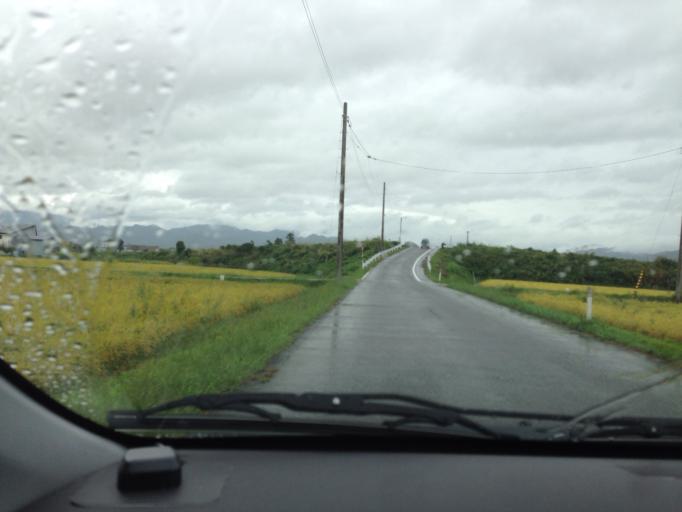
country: JP
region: Fukushima
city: Kitakata
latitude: 37.5102
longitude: 139.8301
